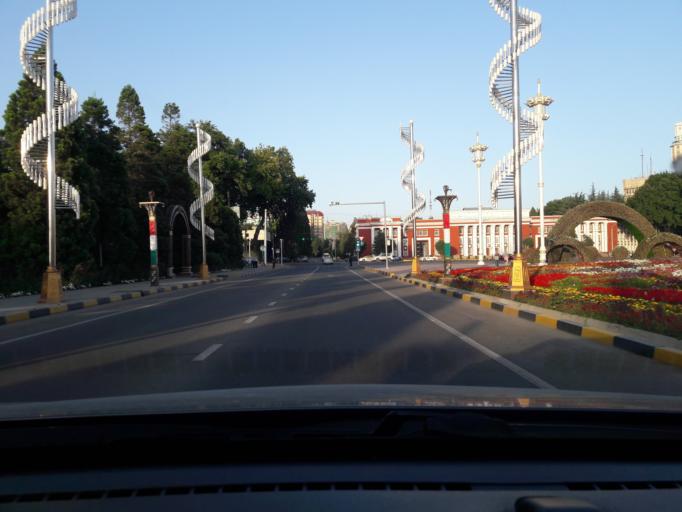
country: TJ
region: Dushanbe
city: Dushanbe
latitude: 38.5745
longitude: 68.7852
